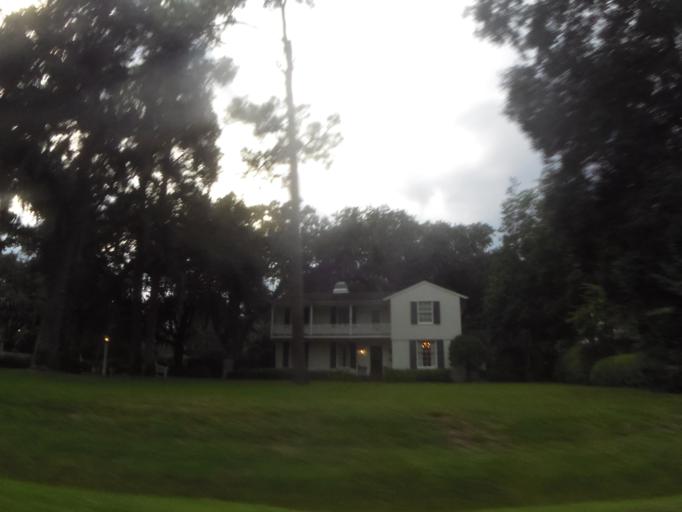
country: US
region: Florida
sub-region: Duval County
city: Jacksonville
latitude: 30.2606
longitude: -81.6978
